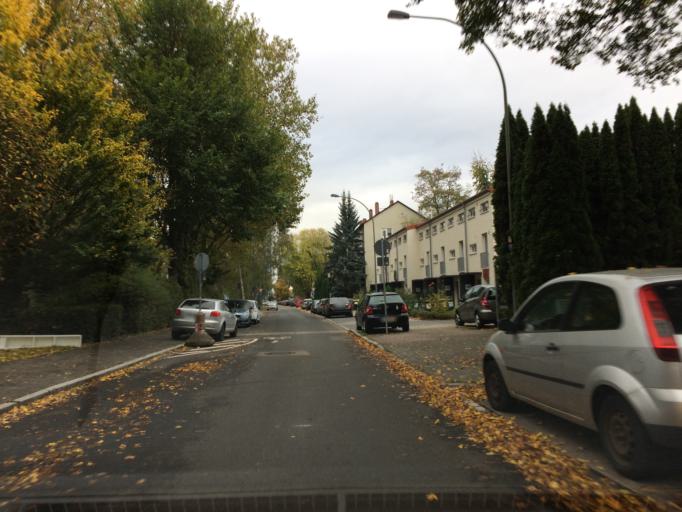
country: DE
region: Hesse
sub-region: Regierungsbezirk Darmstadt
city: Eschborn
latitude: 50.1186
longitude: 8.5548
